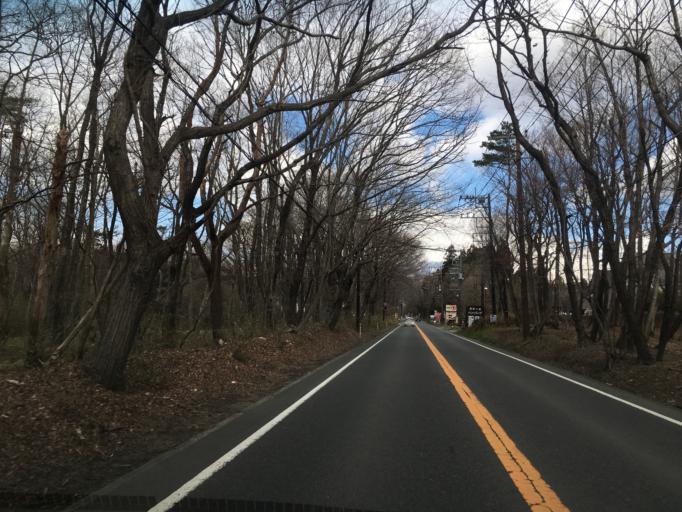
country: JP
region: Tochigi
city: Kuroiso
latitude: 37.0361
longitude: 140.0182
